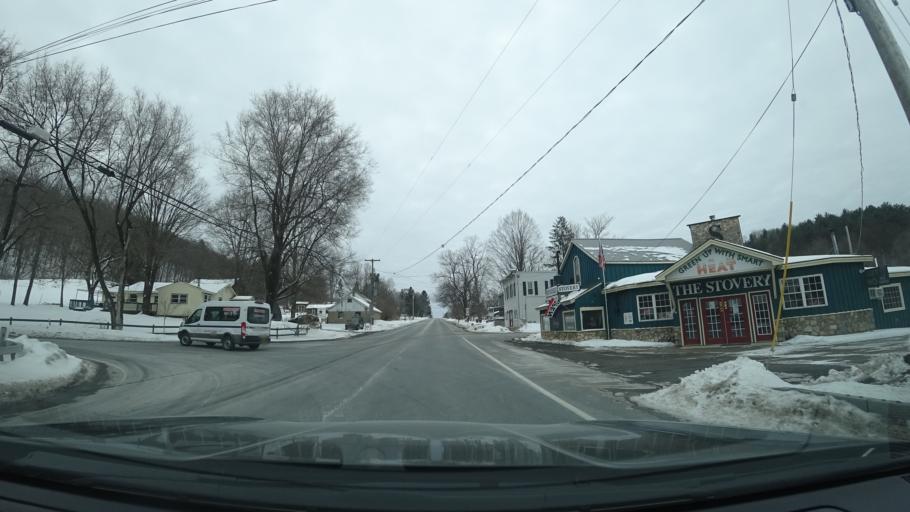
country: US
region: New York
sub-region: Washington County
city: Greenwich
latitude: 43.1850
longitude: -73.4933
